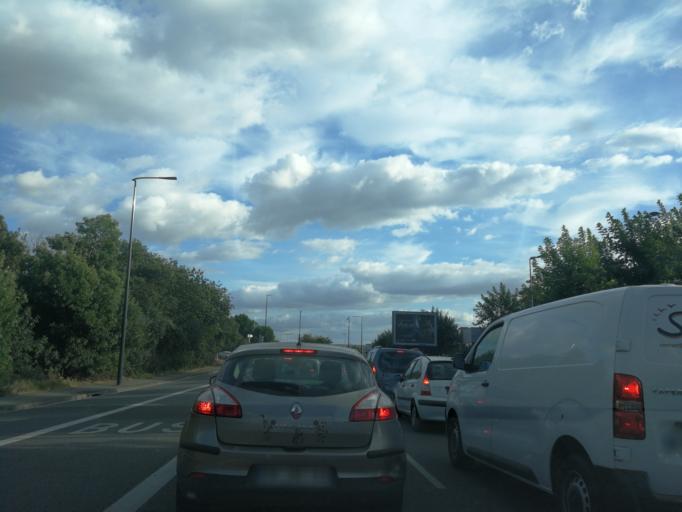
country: FR
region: Midi-Pyrenees
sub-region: Departement de la Haute-Garonne
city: Balma
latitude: 43.6281
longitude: 1.4769
